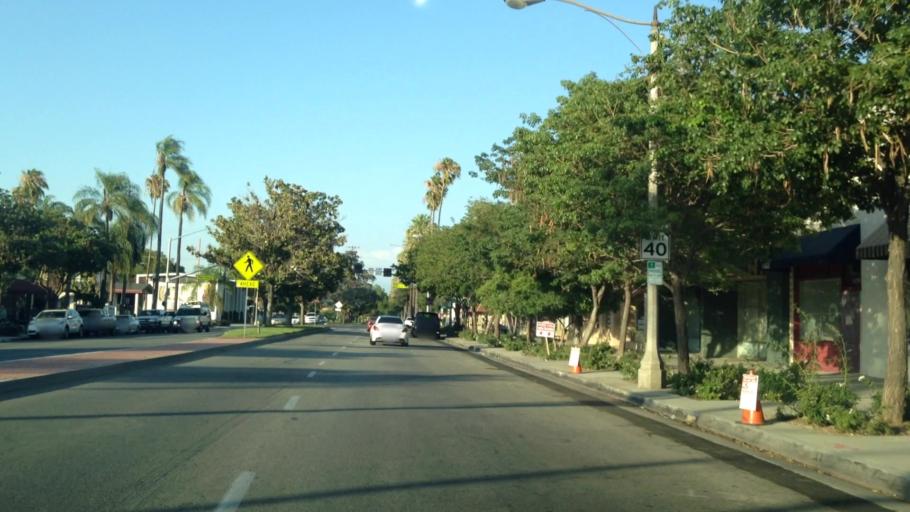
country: US
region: California
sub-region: Riverside County
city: Riverside
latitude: 33.9206
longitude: -117.4461
